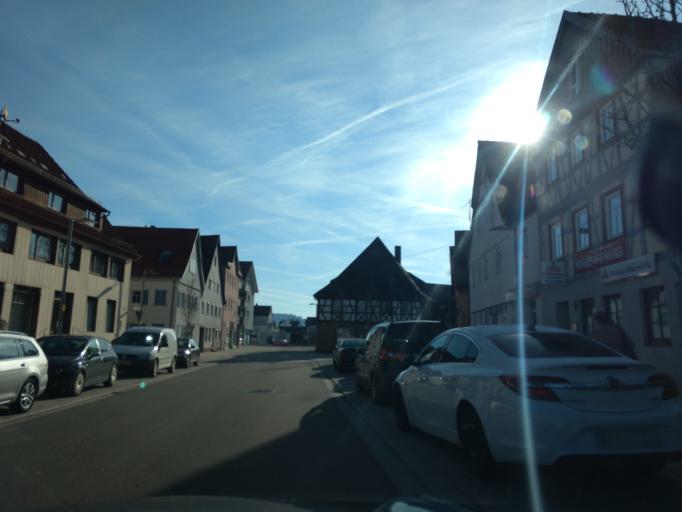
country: DE
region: Baden-Wuerttemberg
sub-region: Regierungsbezirk Stuttgart
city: Lorch
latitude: 48.7972
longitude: 9.6863
